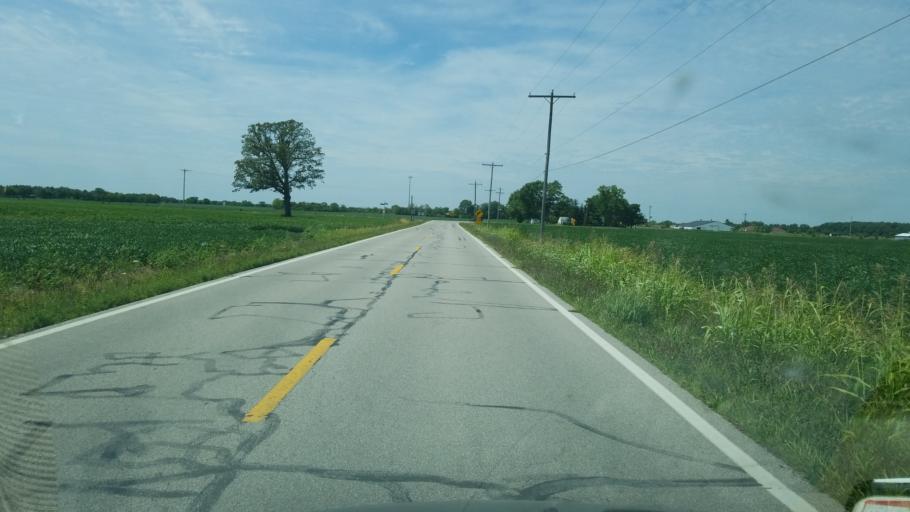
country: US
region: Ohio
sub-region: Franklin County
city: Lake Darby
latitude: 39.8759
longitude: -83.1913
